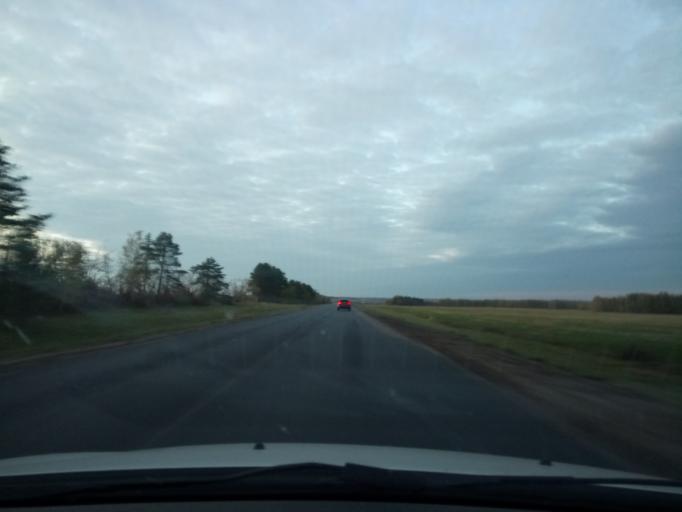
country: RU
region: Nizjnij Novgorod
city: Bol'shoye Murashkino
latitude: 55.8592
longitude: 44.7486
